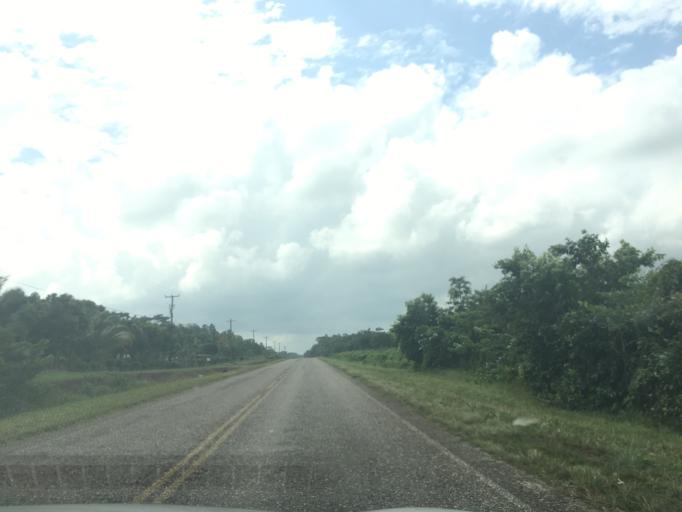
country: BZ
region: Stann Creek
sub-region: Dangriga
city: Dangriga
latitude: 16.9678
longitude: -88.3064
